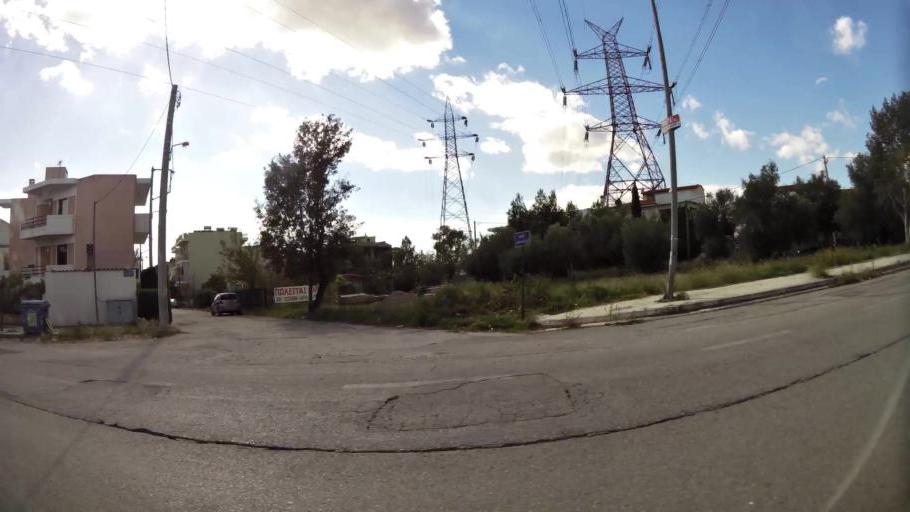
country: GR
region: Attica
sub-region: Nomarchia Anatolikis Attikis
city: Acharnes
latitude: 38.1039
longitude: 23.7390
